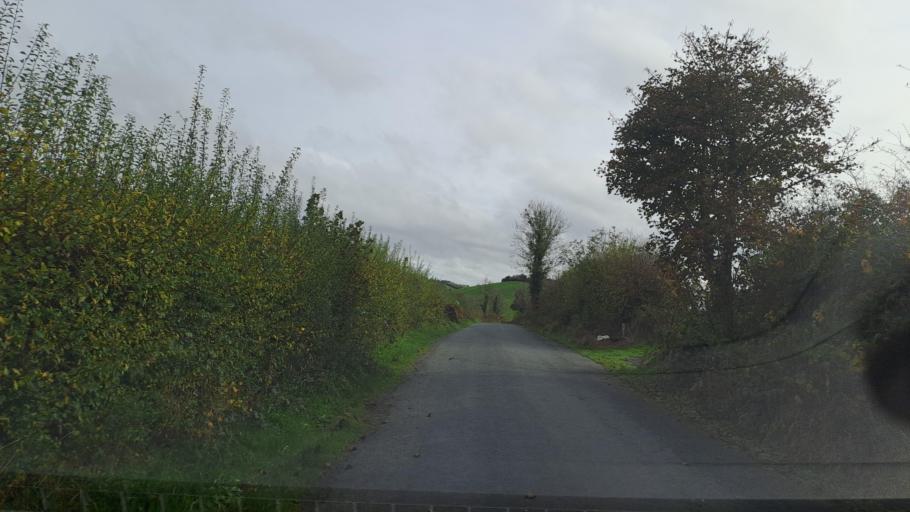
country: IE
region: Ulster
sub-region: An Cabhan
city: Bailieborough
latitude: 54.0228
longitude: -6.9219
